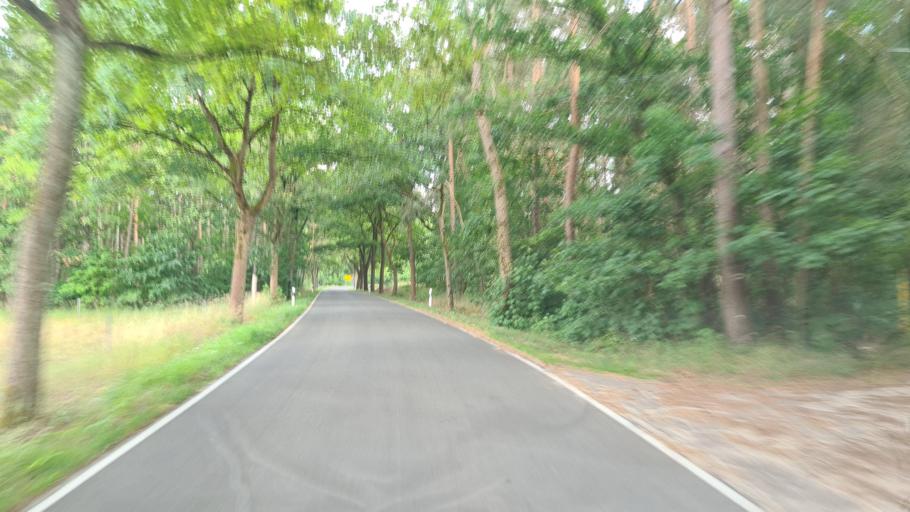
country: DE
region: Saxony-Anhalt
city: Kropstadt
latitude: 51.9350
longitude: 12.7102
